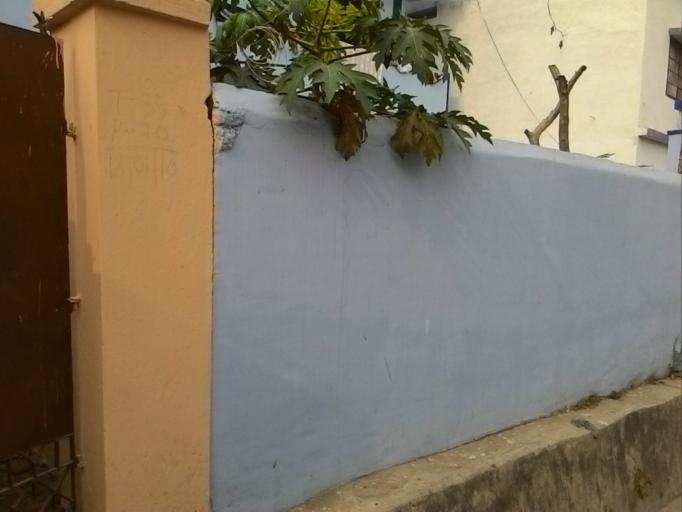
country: IN
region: Jharkhand
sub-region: Giridih
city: Giridih
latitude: 24.1908
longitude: 86.3142
